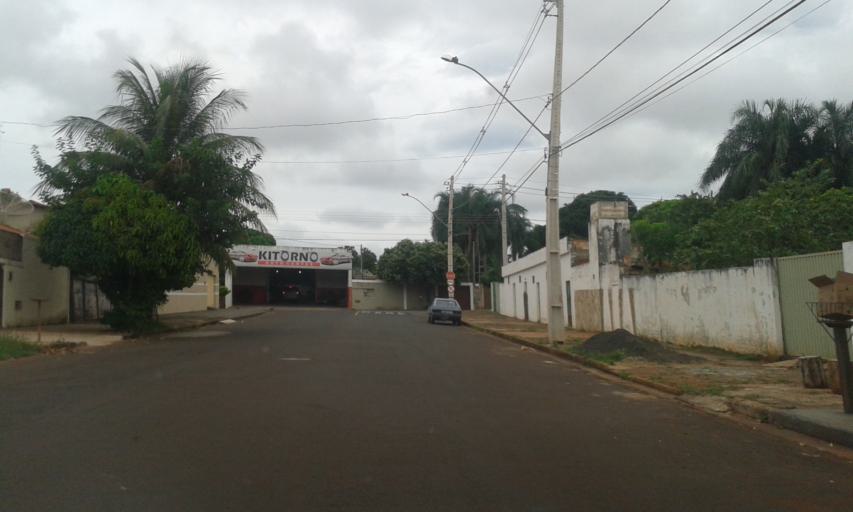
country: BR
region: Minas Gerais
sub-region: Ituiutaba
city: Ituiutaba
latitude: -18.9770
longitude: -49.4514
